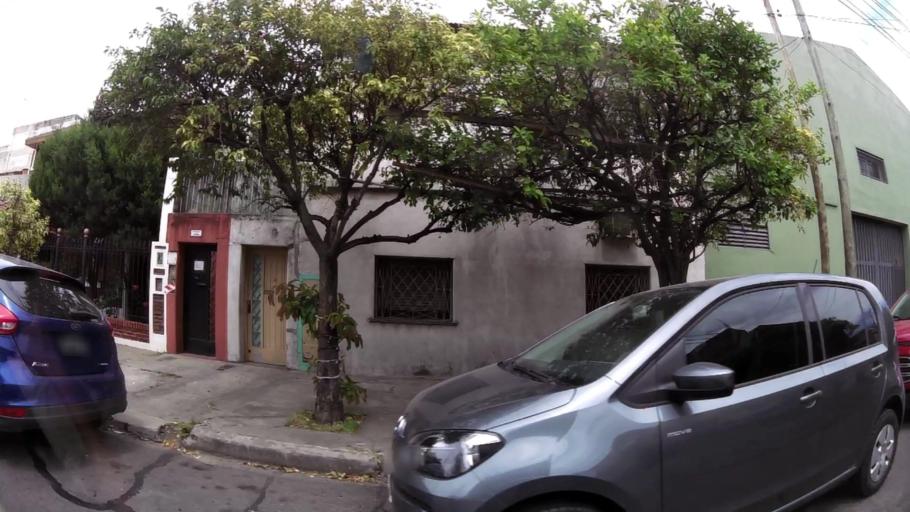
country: AR
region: Buenos Aires
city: San Justo
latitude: -34.6760
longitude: -58.5424
